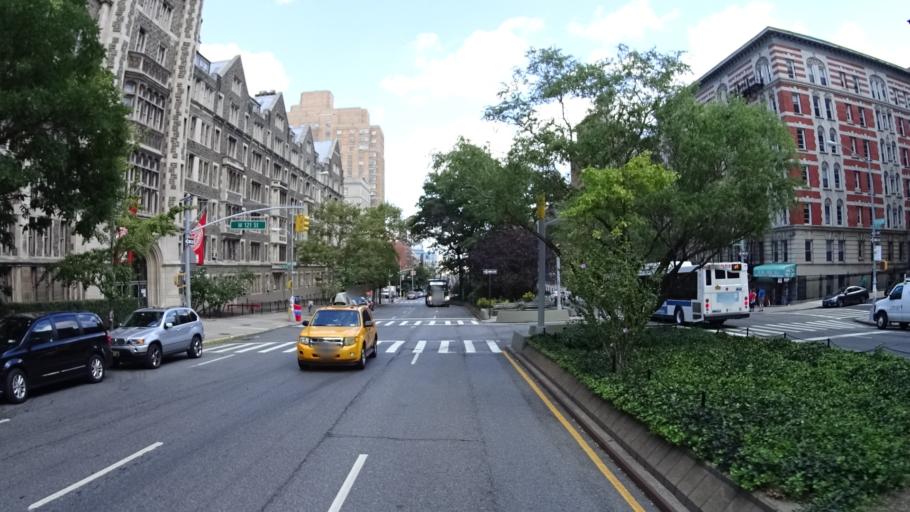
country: US
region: New Jersey
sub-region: Bergen County
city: Edgewater
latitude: 40.8111
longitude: -73.9618
